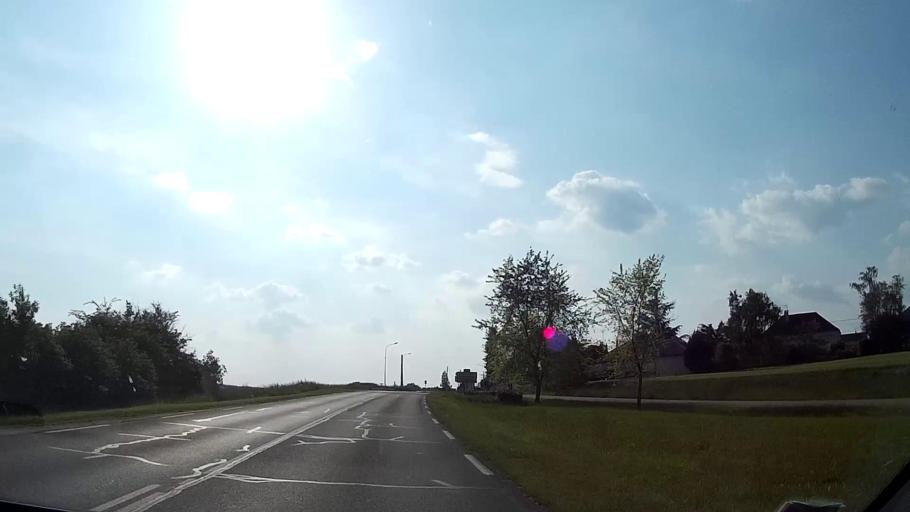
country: FR
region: Centre
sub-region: Departement du Loir-et-Cher
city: Saint-Sulpice-de-Pommeray
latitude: 47.6062
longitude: 1.2785
